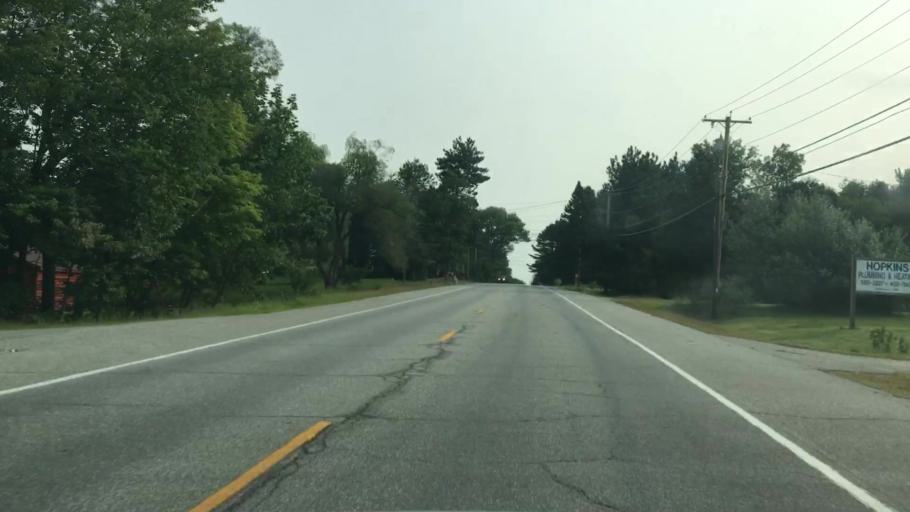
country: US
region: Maine
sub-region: Kennebec County
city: Gardiner
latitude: 44.1902
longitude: -69.8139
